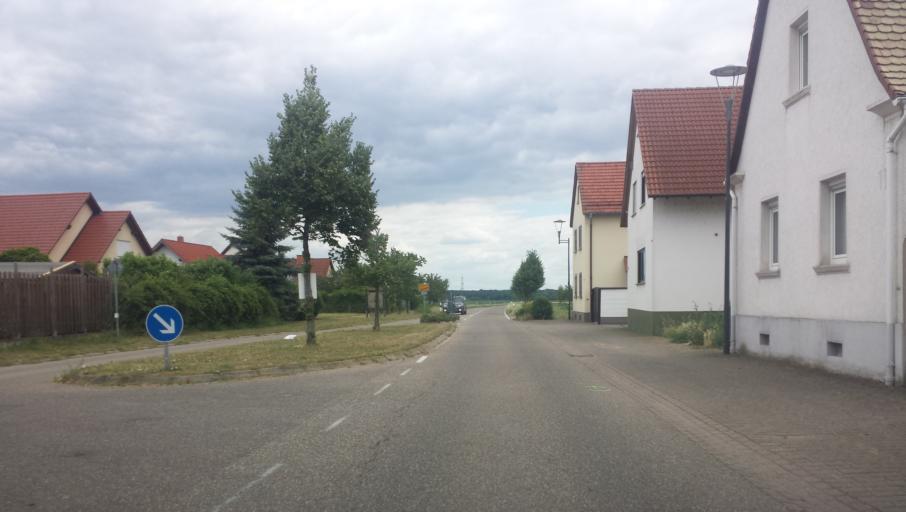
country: DE
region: Rheinland-Pfalz
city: Gommersheim
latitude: 49.2915
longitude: 8.2750
